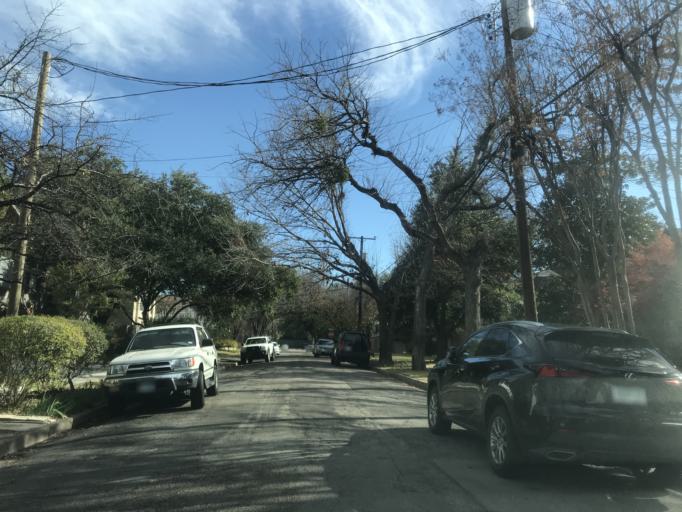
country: US
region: Texas
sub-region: Dallas County
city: Highland Park
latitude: 32.8196
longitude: -96.7969
